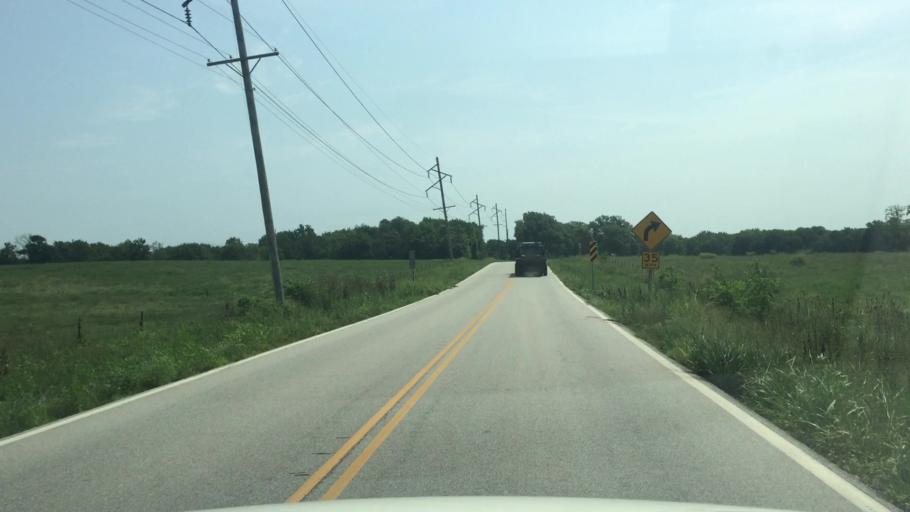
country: US
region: Kansas
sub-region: Montgomery County
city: Cherryvale
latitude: 37.2081
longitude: -95.5616
